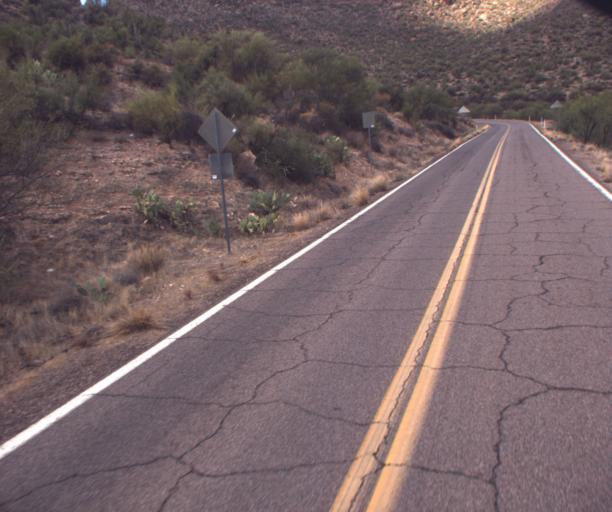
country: US
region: Arizona
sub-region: Pinal County
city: Apache Junction
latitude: 33.5363
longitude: -111.3759
